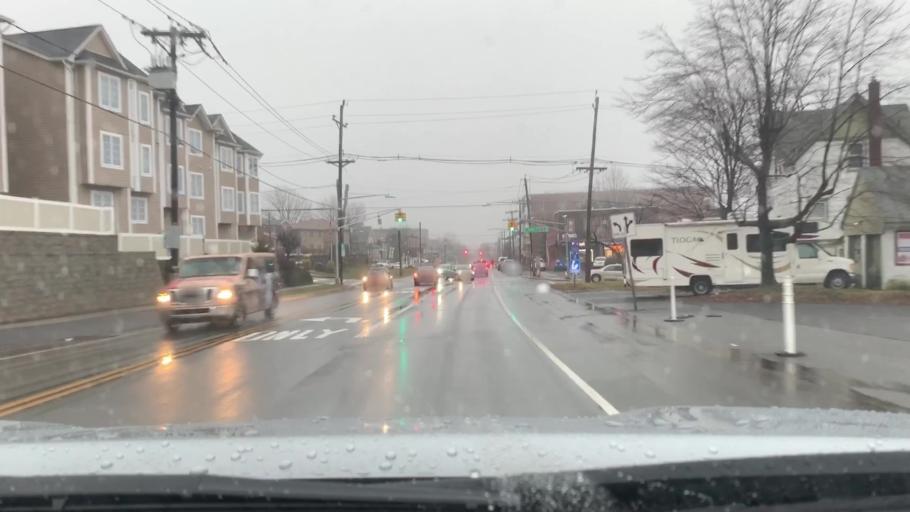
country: US
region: New Jersey
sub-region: Bergen County
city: Palisades Park
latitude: 40.8431
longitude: -73.9873
